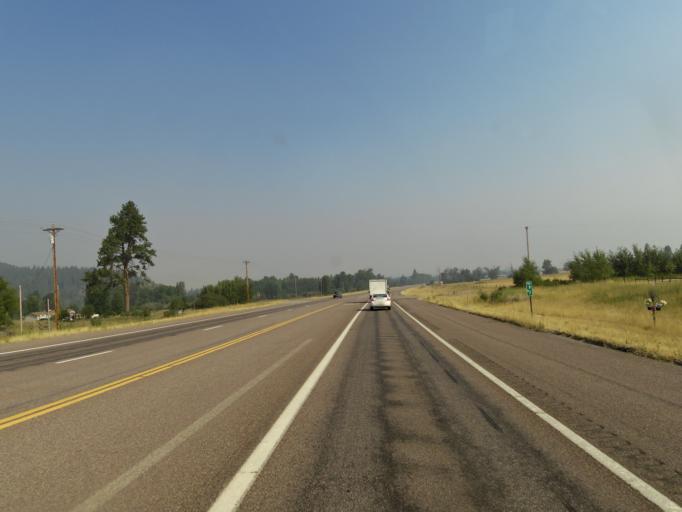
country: US
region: Montana
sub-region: Missoula County
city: Frenchtown
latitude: 47.1084
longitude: -114.0463
